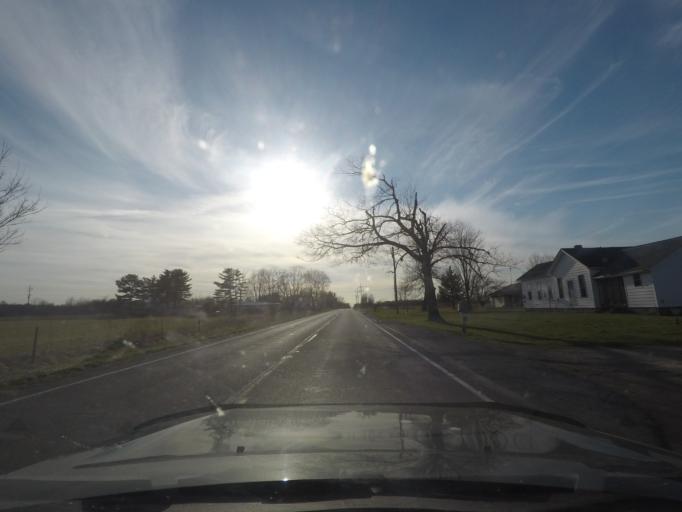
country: US
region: Indiana
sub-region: Saint Joseph County
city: Walkerton
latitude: 41.4482
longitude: -86.4041
